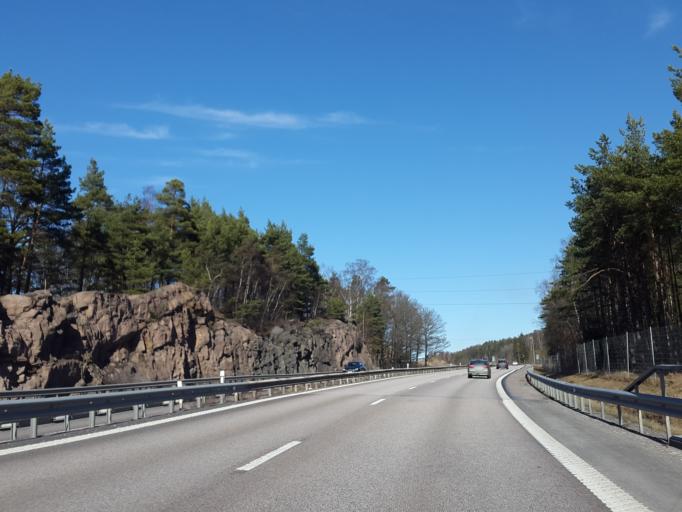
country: SE
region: Vaestra Goetaland
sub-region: Alingsas Kommun
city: Alingsas
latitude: 57.9086
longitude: 12.5043
